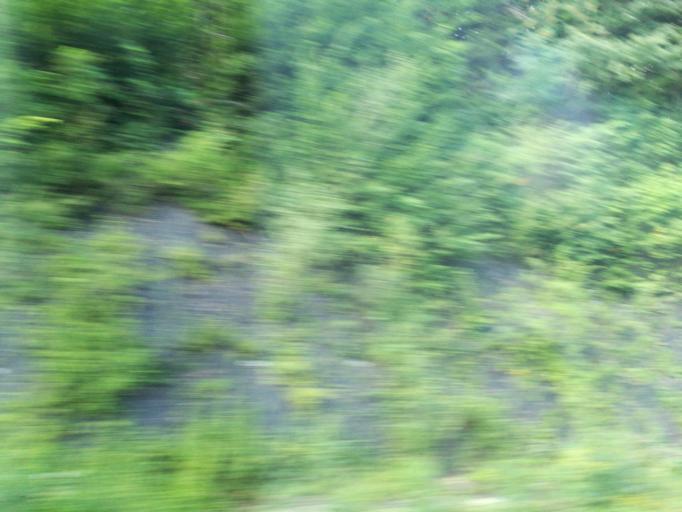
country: RO
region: Prahova
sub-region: Comuna Comarnic
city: Posada
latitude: 45.2885
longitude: 25.6110
